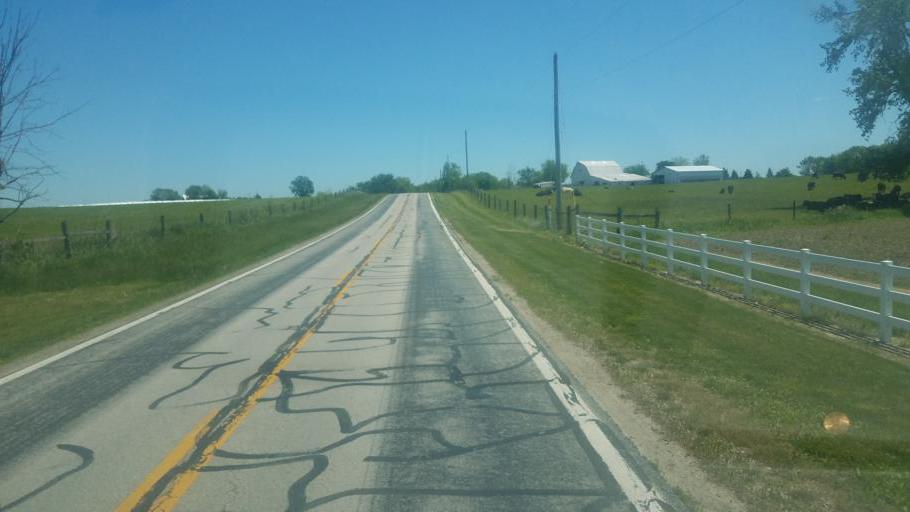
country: US
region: Ohio
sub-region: Darke County
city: Versailles
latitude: 40.2496
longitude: -84.5288
